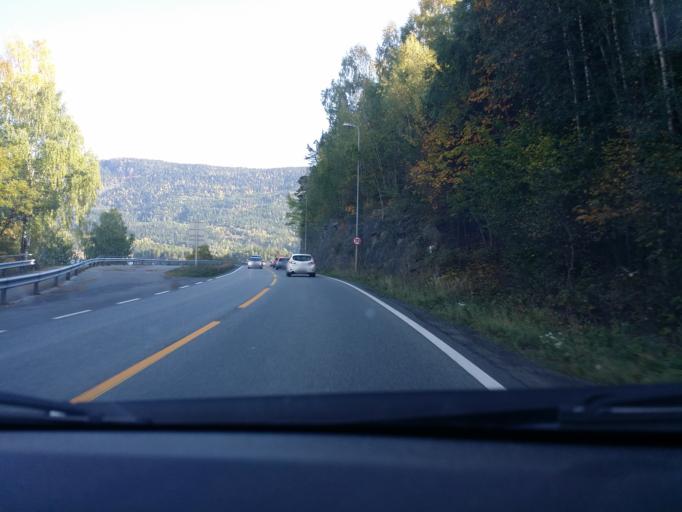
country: NO
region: Buskerud
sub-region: Hole
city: Vik
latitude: 60.0761
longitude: 10.2948
